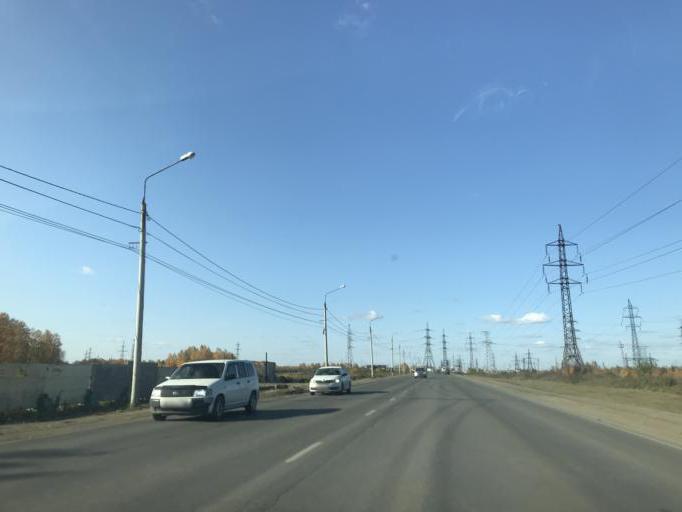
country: RU
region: Chelyabinsk
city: Roshchino
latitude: 55.2219
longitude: 61.2950
